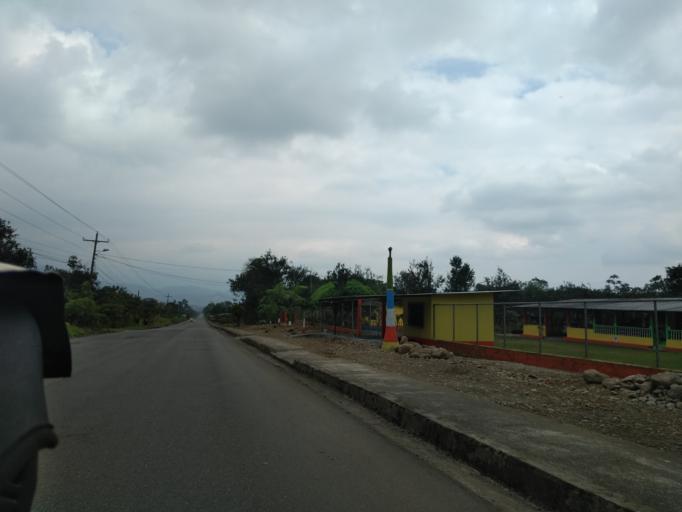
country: EC
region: Cotopaxi
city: La Mana
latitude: -0.8777
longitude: -79.1604
